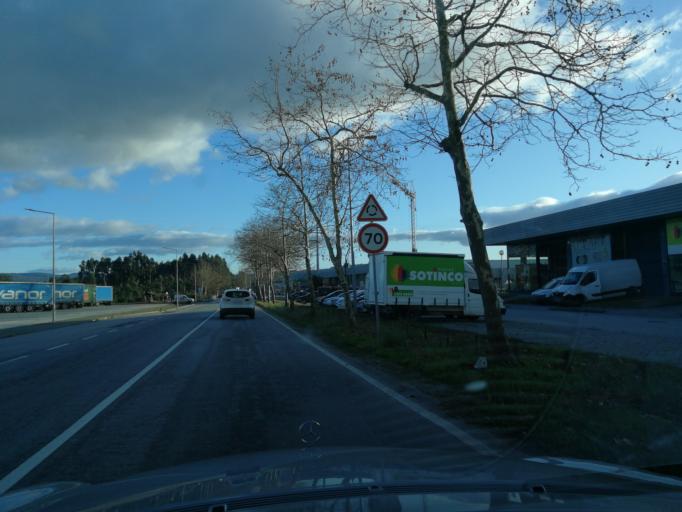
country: PT
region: Viana do Castelo
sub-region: Viana do Castelo
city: Darque
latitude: 41.6344
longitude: -8.7644
